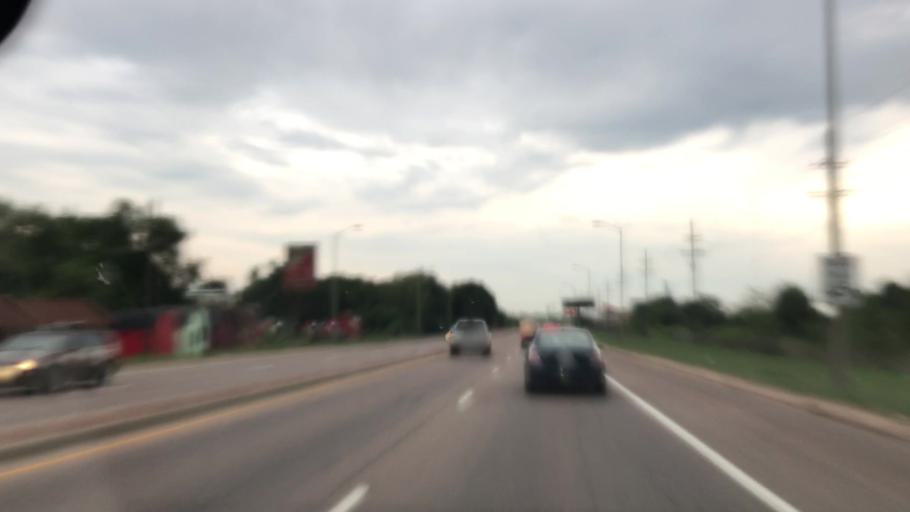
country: US
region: Colorado
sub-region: El Paso County
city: Colorado Springs
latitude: 38.8342
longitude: -104.8467
